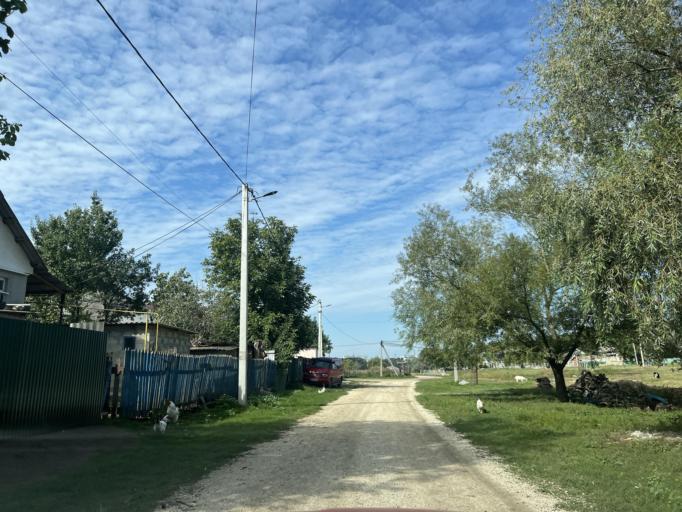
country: MD
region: Ungheni
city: Ungheni
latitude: 47.1962
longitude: 27.8121
